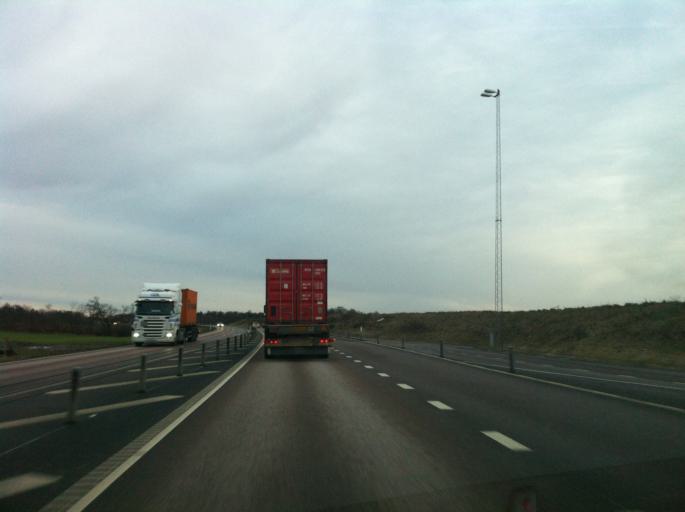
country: SE
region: Skane
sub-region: Helsingborg
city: Helsingborg
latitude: 56.0992
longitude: 12.6678
